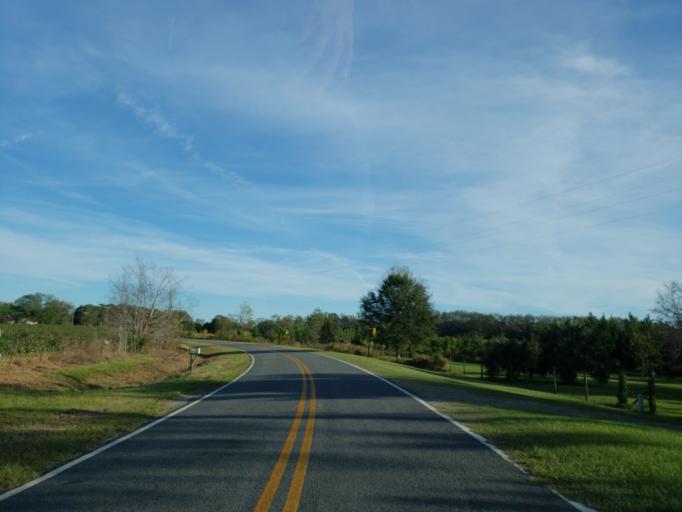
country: US
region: Georgia
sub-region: Dooly County
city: Vienna
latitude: 32.0334
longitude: -83.7518
